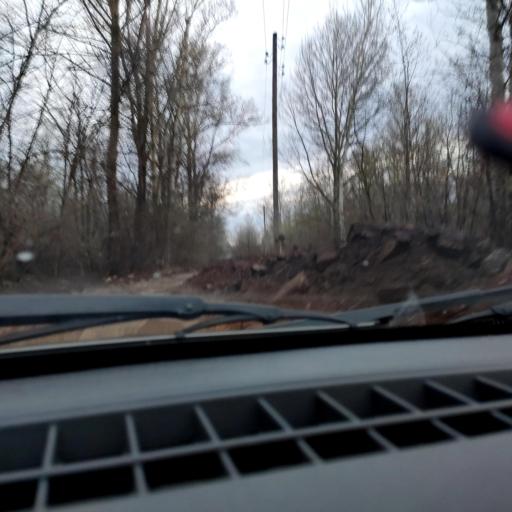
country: RU
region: Bashkortostan
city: Ufa
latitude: 54.6782
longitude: 55.9510
